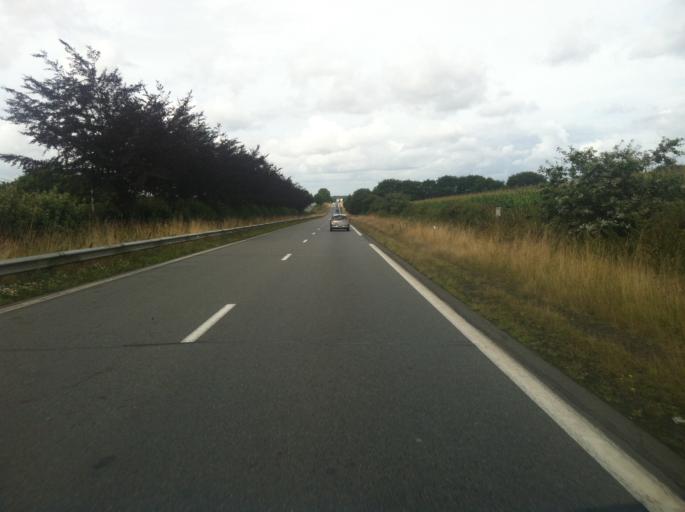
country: FR
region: Brittany
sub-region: Departement du Finistere
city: Lampaul-Guimiliau
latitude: 48.5202
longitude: -4.0075
